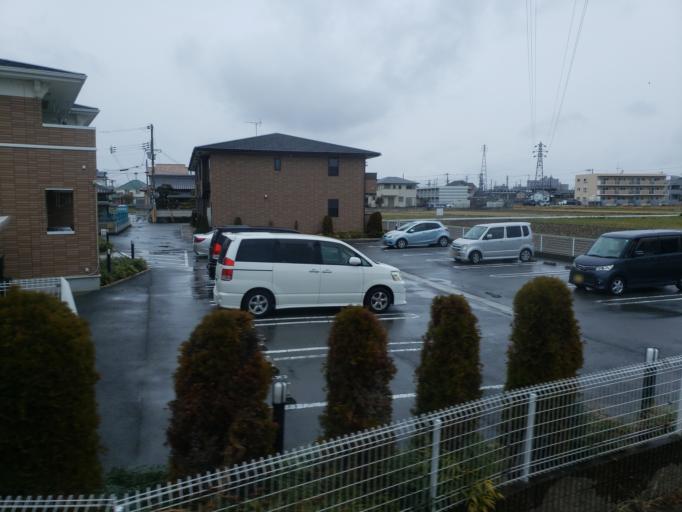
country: JP
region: Hyogo
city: Kakogawacho-honmachi
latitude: 34.7087
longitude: 134.8752
